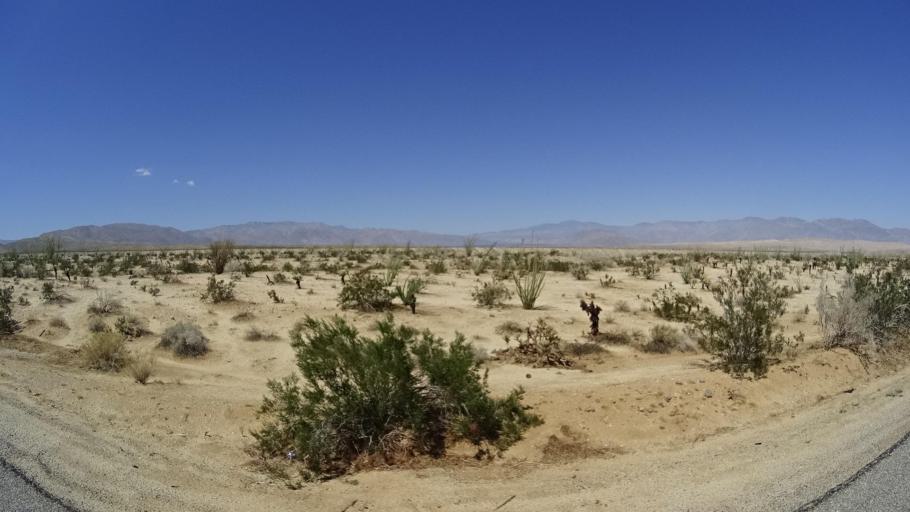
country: US
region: California
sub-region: San Diego County
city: Borrego Springs
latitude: 33.1498
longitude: -116.2589
